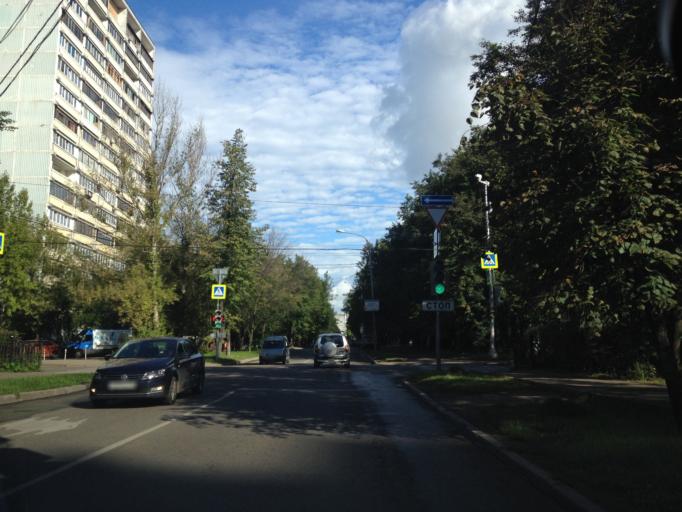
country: RU
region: Moskovskaya
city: Izmaylovo
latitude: 55.7968
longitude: 37.8055
